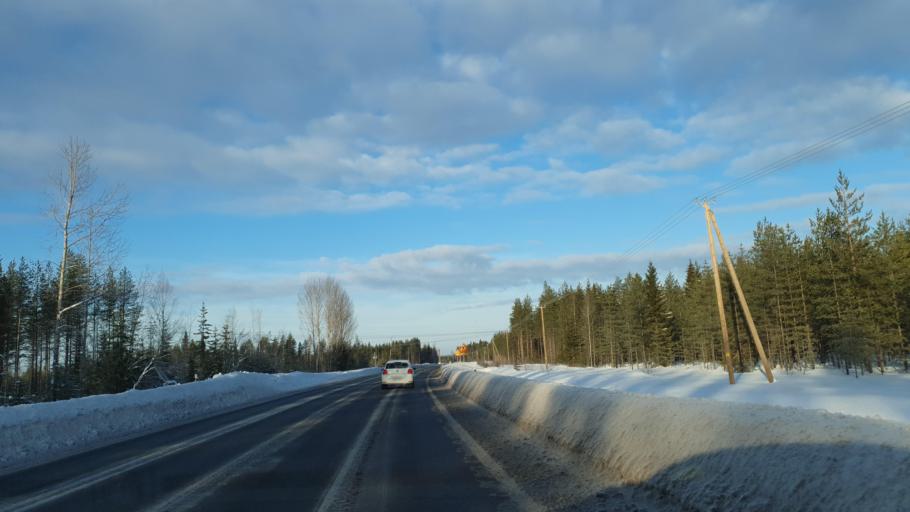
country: FI
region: Northern Ostrobothnia
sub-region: Oulu
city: Muhos
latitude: 64.7844
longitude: 26.1925
